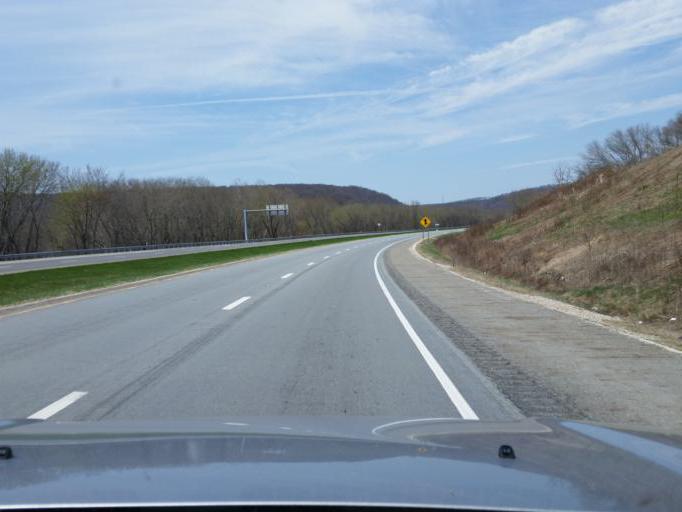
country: US
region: Pennsylvania
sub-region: Perry County
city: Newport
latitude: 40.5441
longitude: -77.1517
